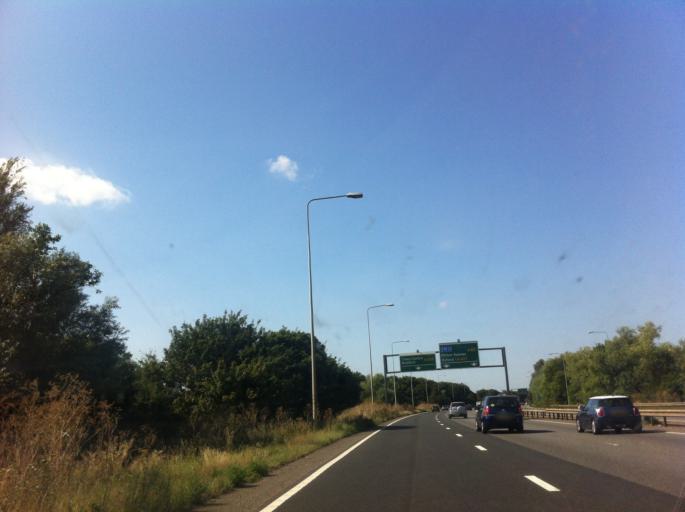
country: GB
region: England
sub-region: Northamptonshire
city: Northampton
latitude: 52.2382
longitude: -0.8471
